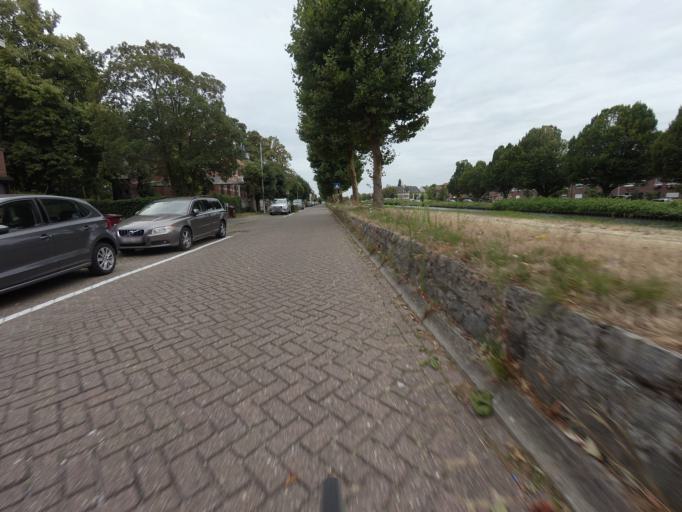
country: BE
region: Flanders
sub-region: Provincie Antwerpen
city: Schoten
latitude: 51.2581
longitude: 4.5105
